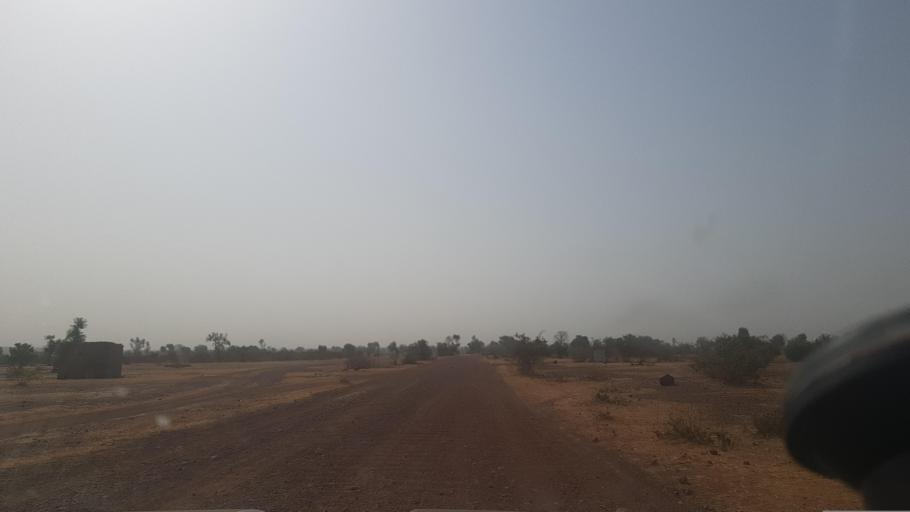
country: ML
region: Segou
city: Baroueli
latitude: 13.1551
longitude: -6.5167
